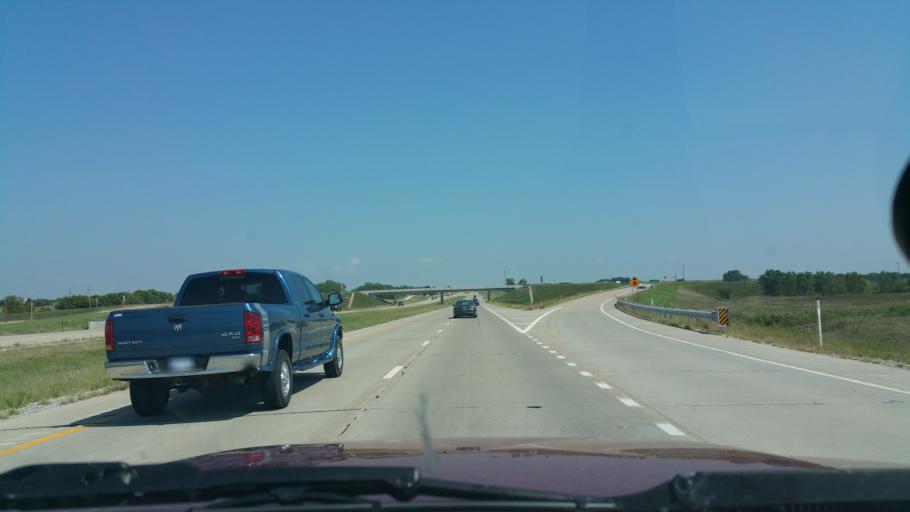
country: US
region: Kansas
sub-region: Dickinson County
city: Abilene
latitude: 38.9438
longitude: -97.1712
